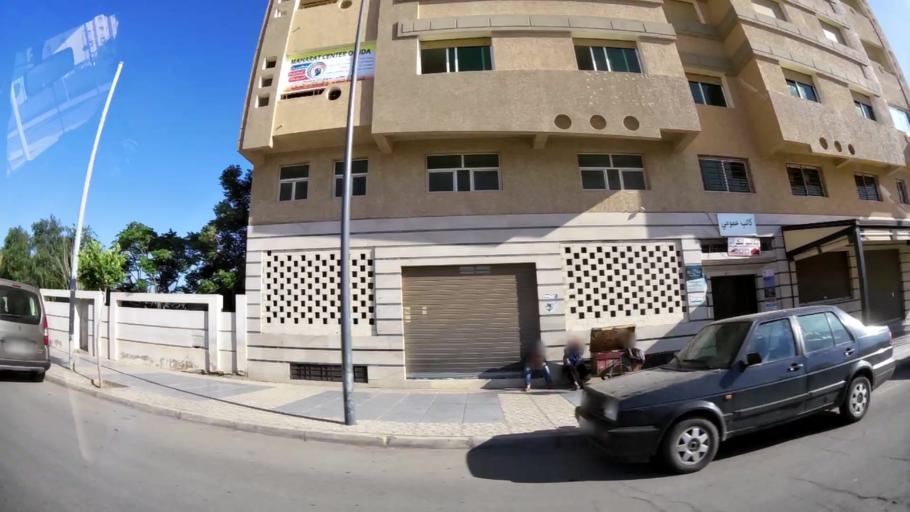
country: MA
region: Oriental
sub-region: Oujda-Angad
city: Oujda
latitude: 34.6913
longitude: -1.9122
